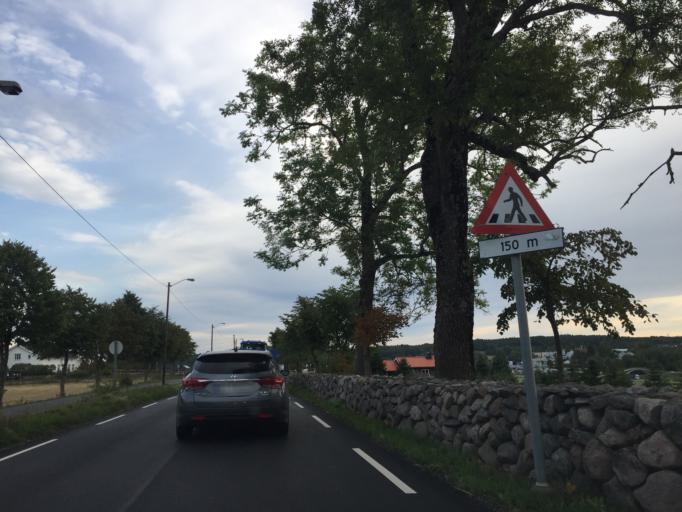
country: NO
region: Akershus
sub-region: As
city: As
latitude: 59.7162
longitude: 10.7753
